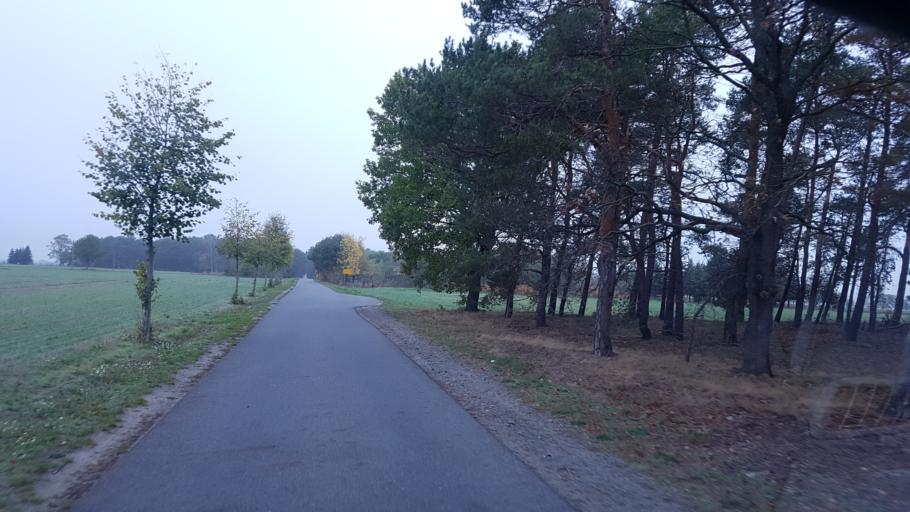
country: DE
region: Brandenburg
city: Sonnewalde
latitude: 51.6734
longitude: 13.6322
